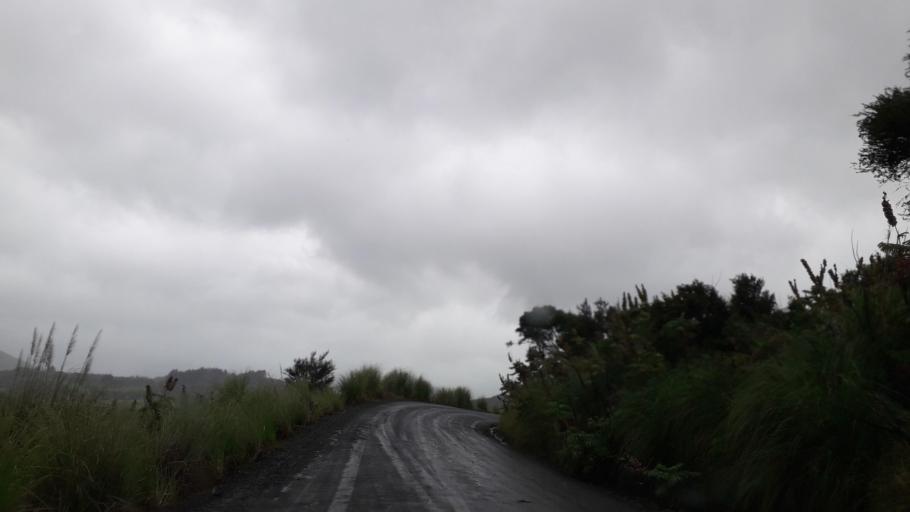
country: NZ
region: Northland
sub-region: Far North District
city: Kaitaia
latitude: -35.4078
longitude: 173.3632
